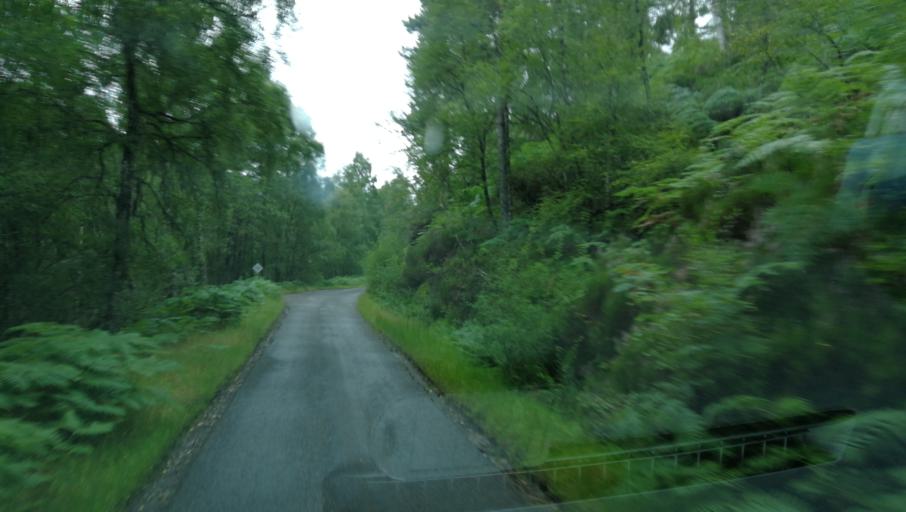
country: GB
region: Scotland
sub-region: Highland
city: Spean Bridge
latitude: 57.3098
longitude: -4.8652
